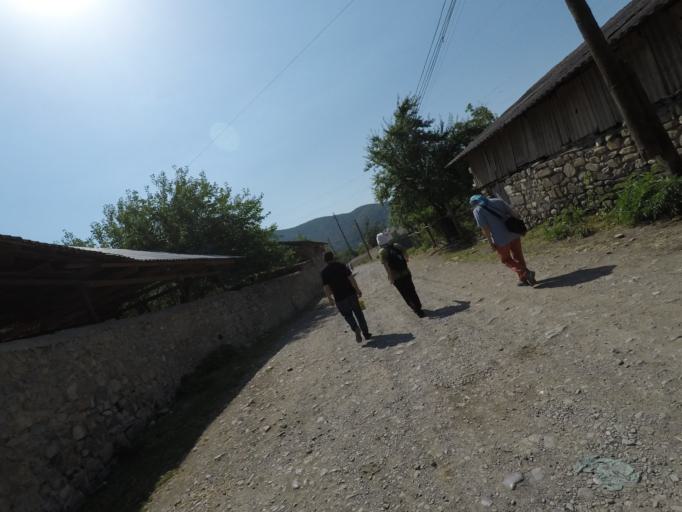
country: AZ
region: Qakh Rayon
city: Cinarli
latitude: 41.4835
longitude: 46.8480
